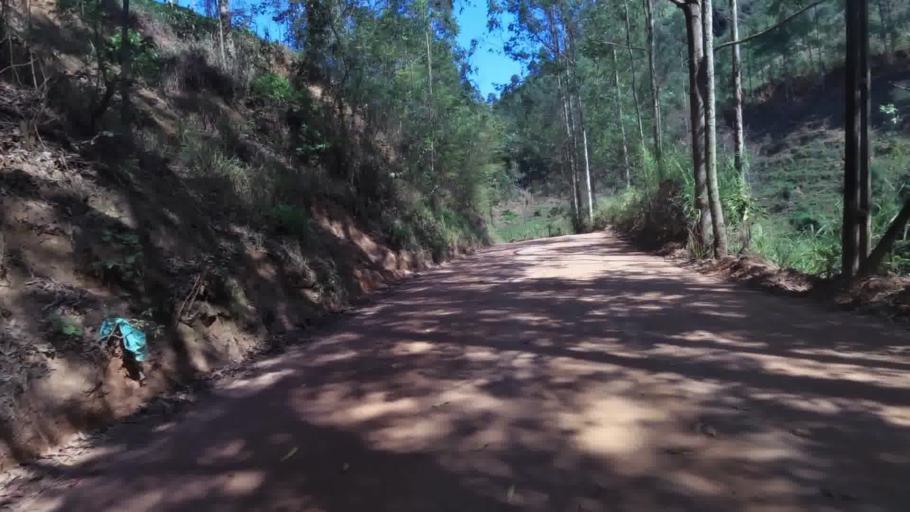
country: BR
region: Espirito Santo
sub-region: Alfredo Chaves
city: Alfredo Chaves
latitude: -20.6516
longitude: -40.8058
